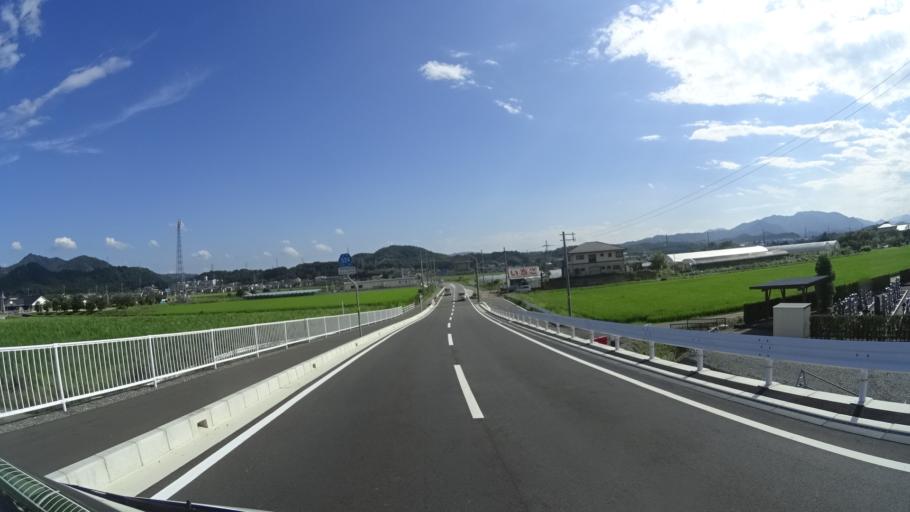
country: JP
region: Kyoto
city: Fukuchiyama
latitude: 35.3077
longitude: 135.1709
